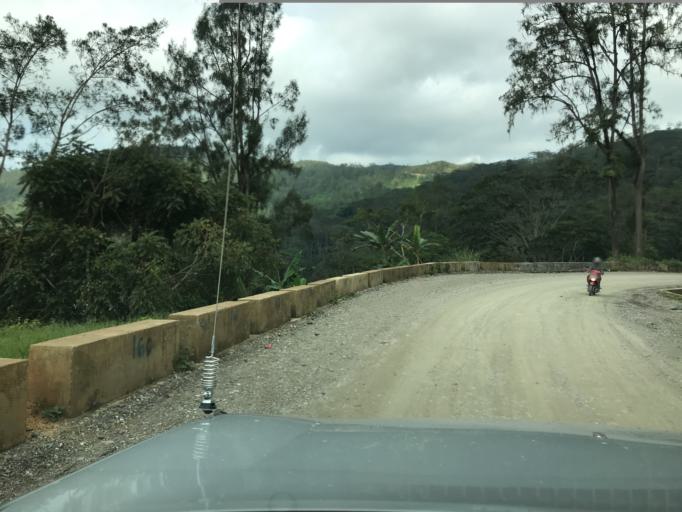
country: TL
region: Aileu
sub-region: Aileu Villa
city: Aileu
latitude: -8.6730
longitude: 125.5498
